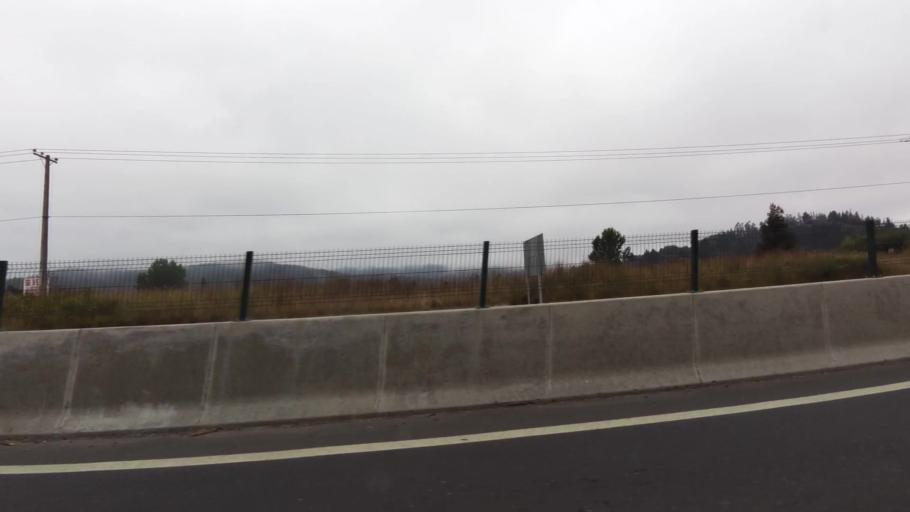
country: CL
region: Biobio
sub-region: Provincia de Concepcion
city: Concepcion
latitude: -36.8153
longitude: -72.9846
